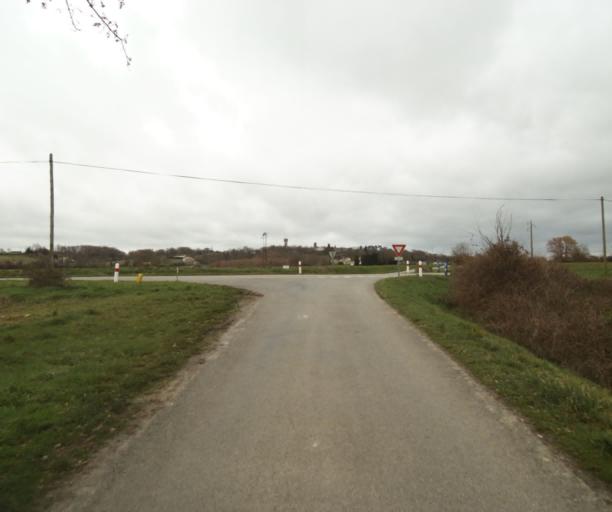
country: FR
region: Midi-Pyrenees
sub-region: Departement de l'Ariege
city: Saverdun
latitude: 43.1875
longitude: 1.6337
